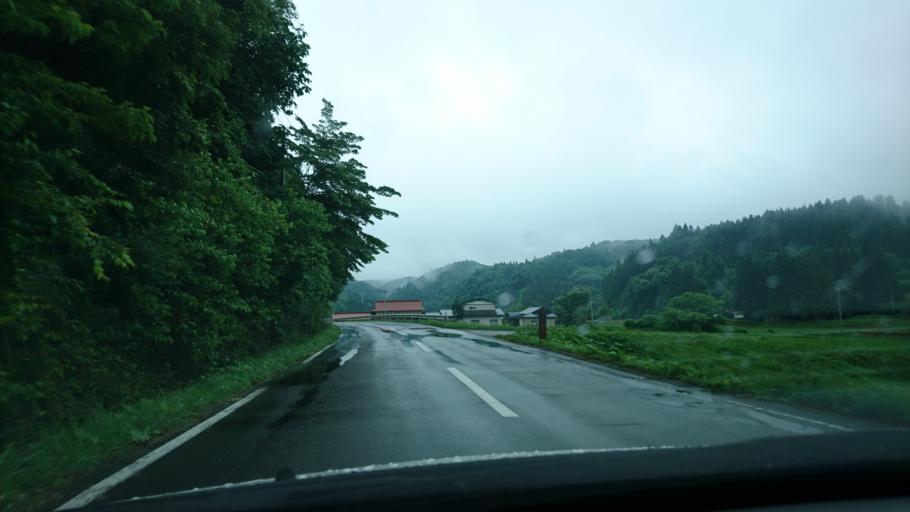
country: JP
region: Iwate
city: Ichinoseki
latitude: 38.9009
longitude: 141.0361
